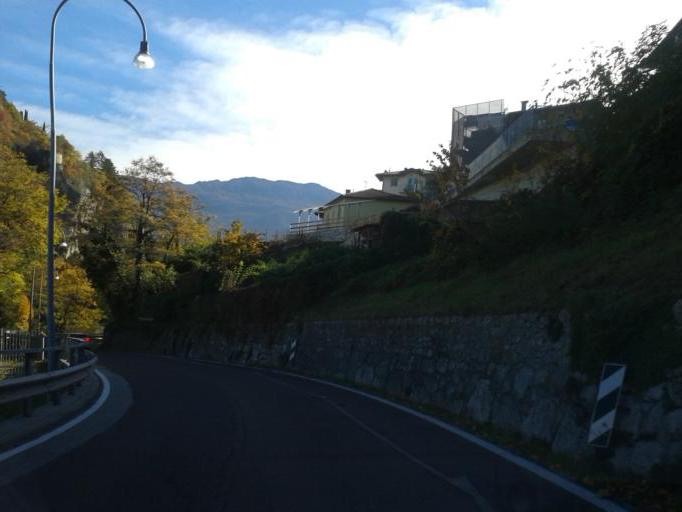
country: IT
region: Trentino-Alto Adige
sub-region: Provincia di Trento
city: Trento
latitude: 46.0729
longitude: 11.1064
